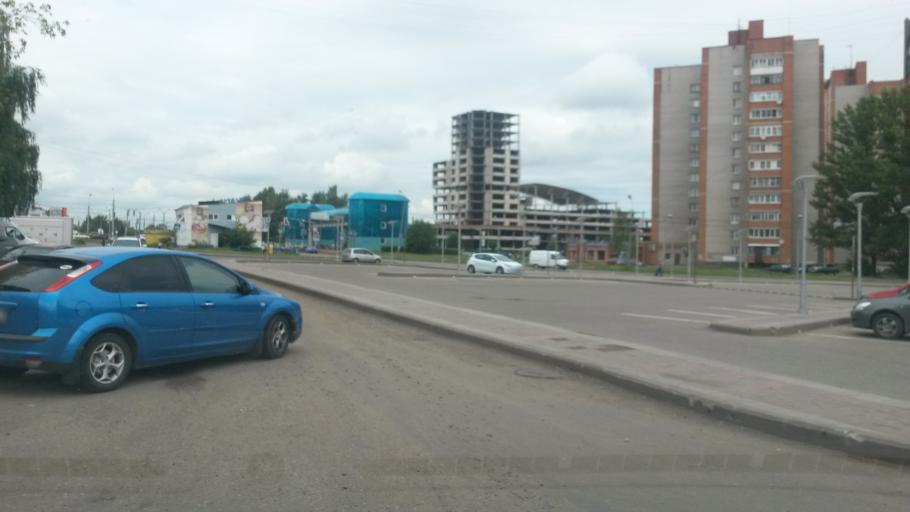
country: RU
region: Jaroslavl
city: Yaroslavl
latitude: 57.5912
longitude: 39.8651
